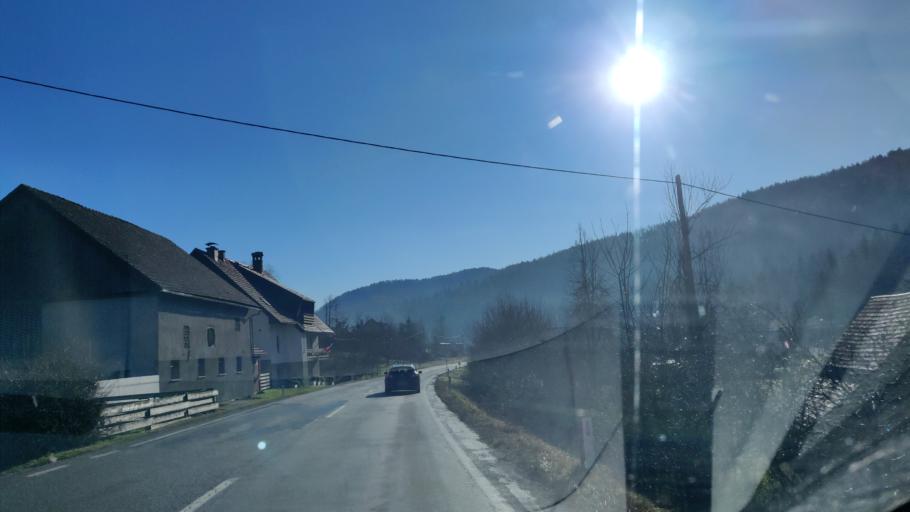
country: SI
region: Logatec
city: Logatec
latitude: 45.8754
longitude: 14.2118
